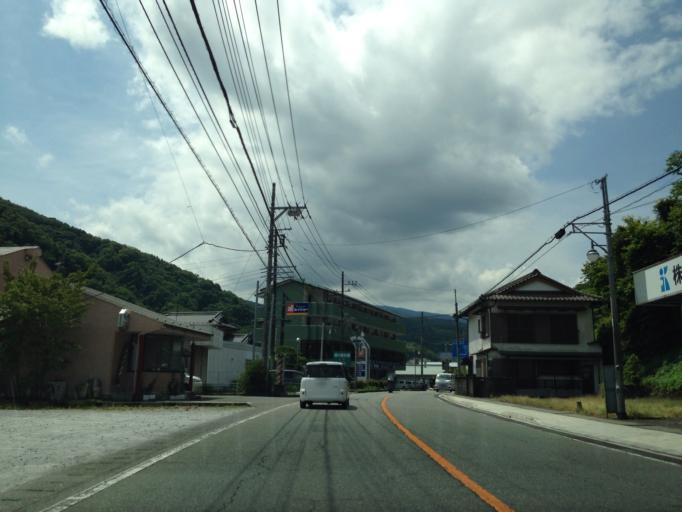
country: JP
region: Shizuoka
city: Heda
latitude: 34.9350
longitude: 138.9332
